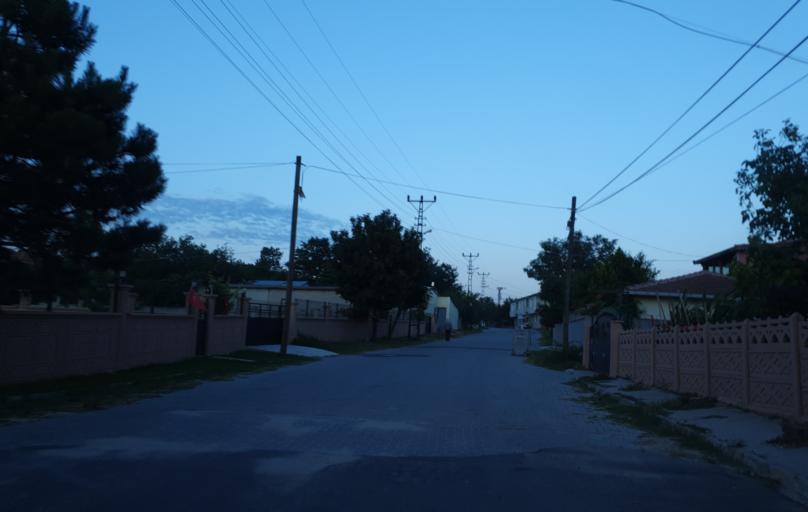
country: TR
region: Tekirdag
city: Velimese
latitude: 41.3490
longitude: 27.8824
